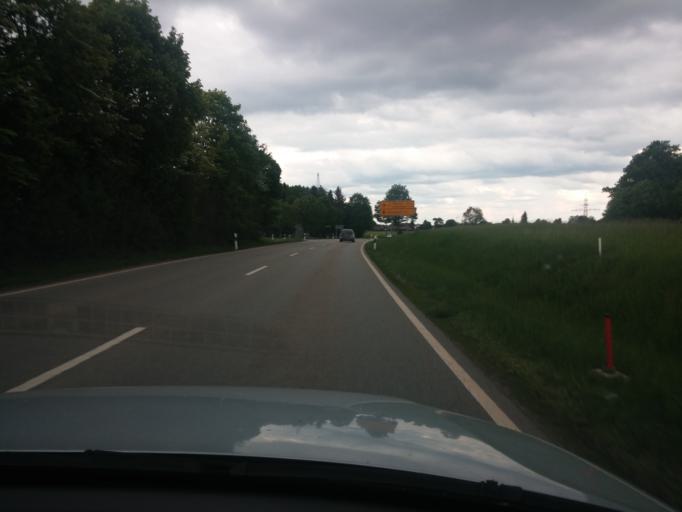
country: DE
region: Bavaria
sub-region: Upper Bavaria
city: Holzkirchen
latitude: 47.8645
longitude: 11.6899
